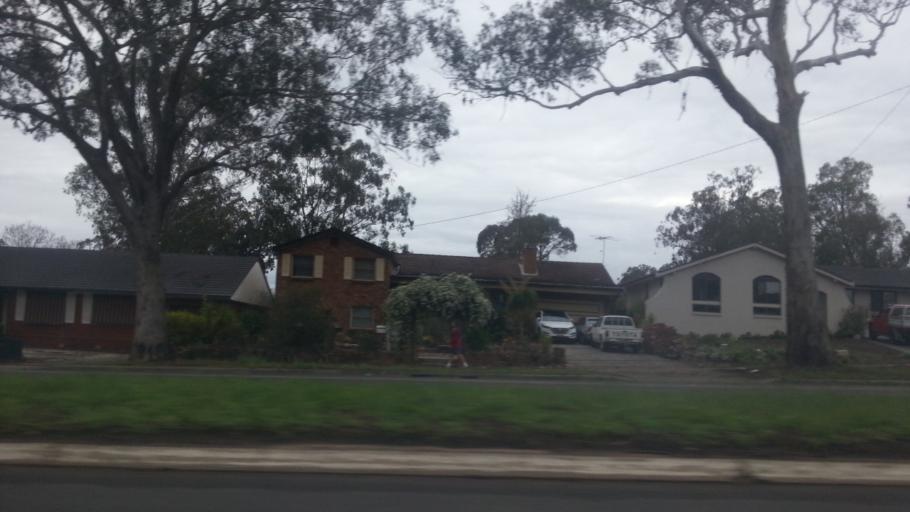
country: AU
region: New South Wales
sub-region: Camden
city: Camden South
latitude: -34.0848
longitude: 150.6949
